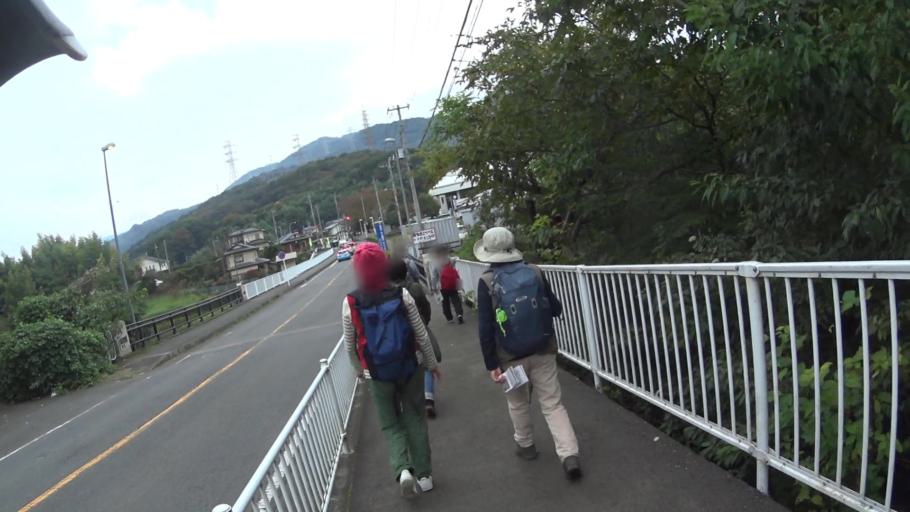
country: JP
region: Kanagawa
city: Hadano
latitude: 35.3961
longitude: 139.2307
